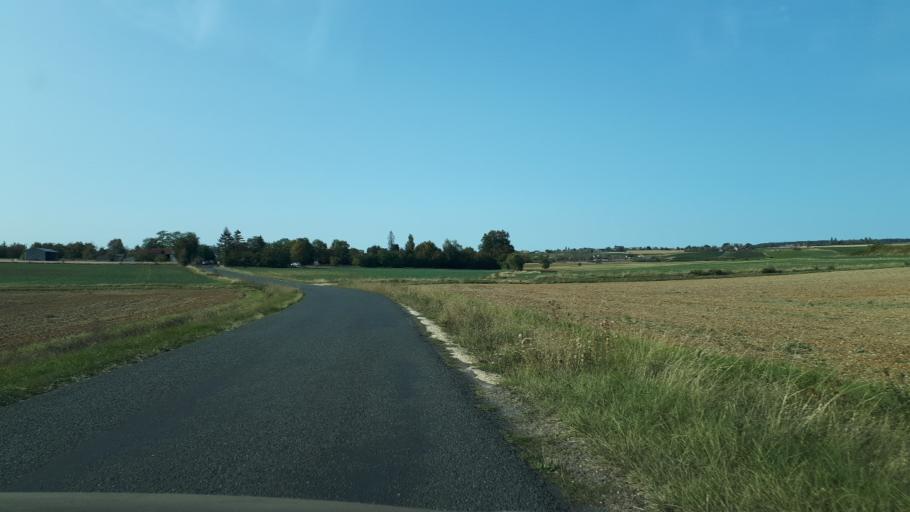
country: FR
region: Centre
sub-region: Departement du Cher
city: Menetou-Salon
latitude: 47.2141
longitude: 2.5516
